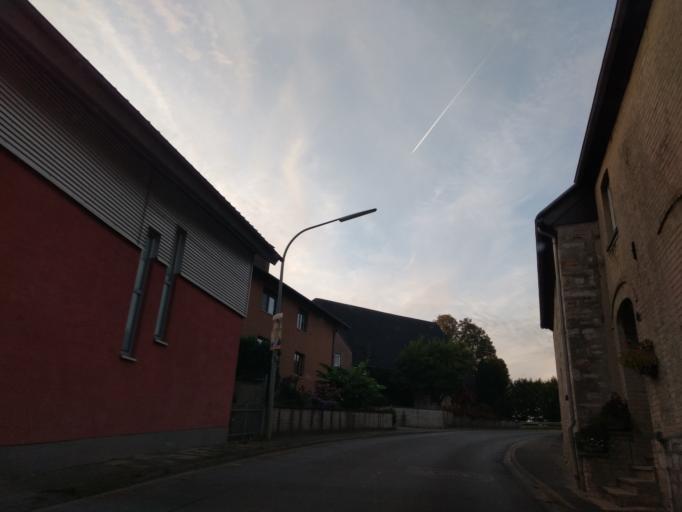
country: DE
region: North Rhine-Westphalia
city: Lichtenau
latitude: 51.6736
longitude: 8.8330
